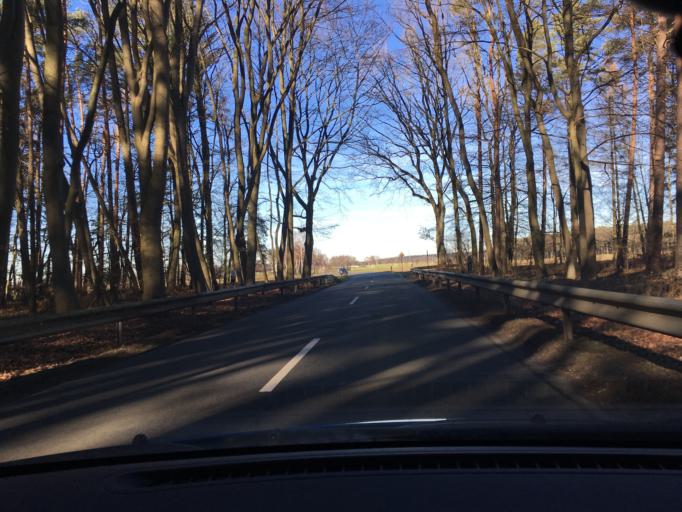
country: DE
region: Lower Saxony
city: Schwienau
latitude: 52.9882
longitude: 10.4441
